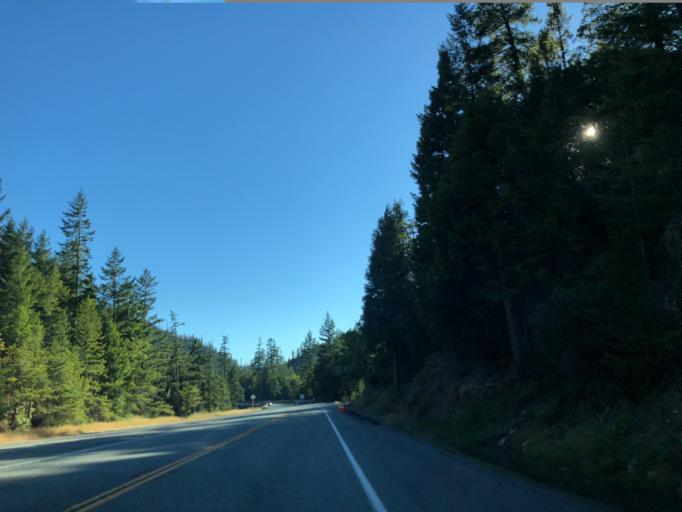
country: US
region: California
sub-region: Del Norte County
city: Bertsch-Oceanview
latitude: 41.8618
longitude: -123.8696
